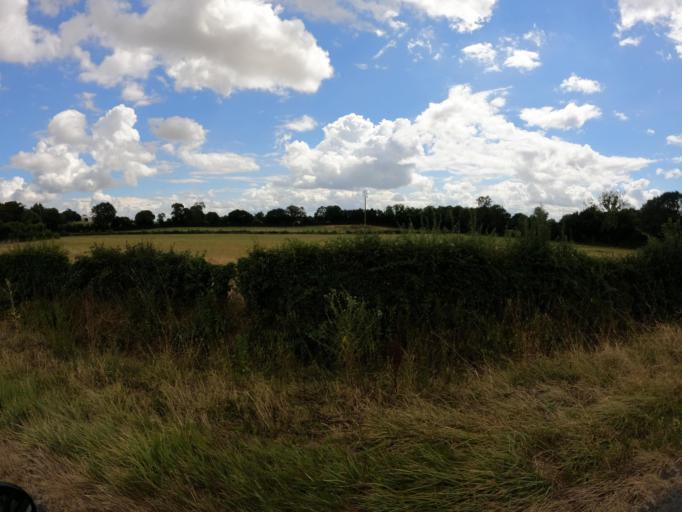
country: FR
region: Pays de la Loire
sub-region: Departement de Maine-et-Loire
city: Mire
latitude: 47.7801
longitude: -0.4640
